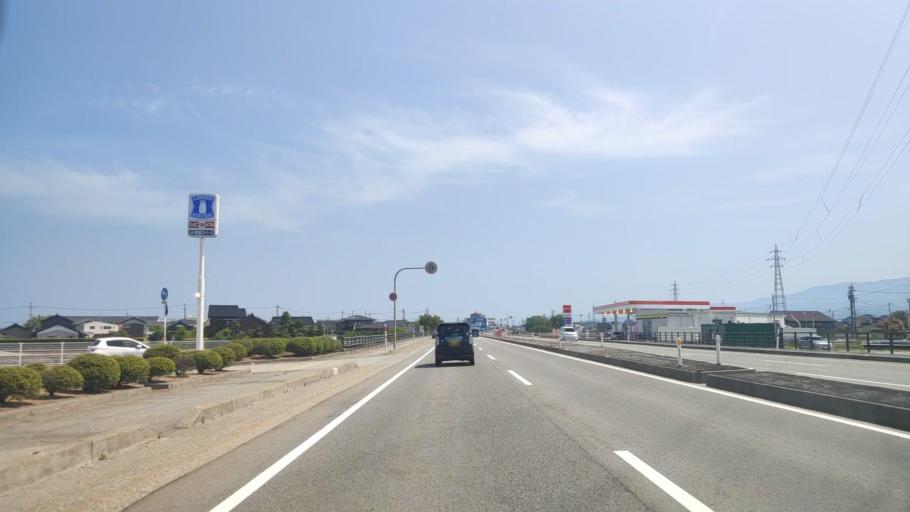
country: JP
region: Toyama
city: Namerikawa
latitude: 36.7467
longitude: 137.3477
